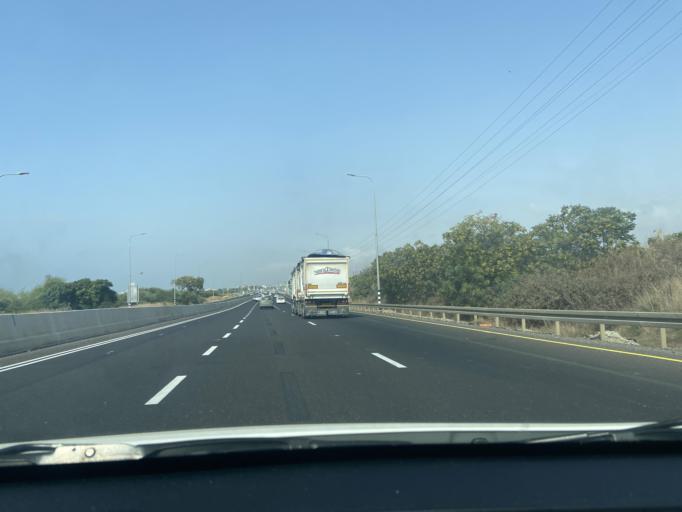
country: IL
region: Northern District
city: El Mazra`a
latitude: 32.9728
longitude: 35.0932
